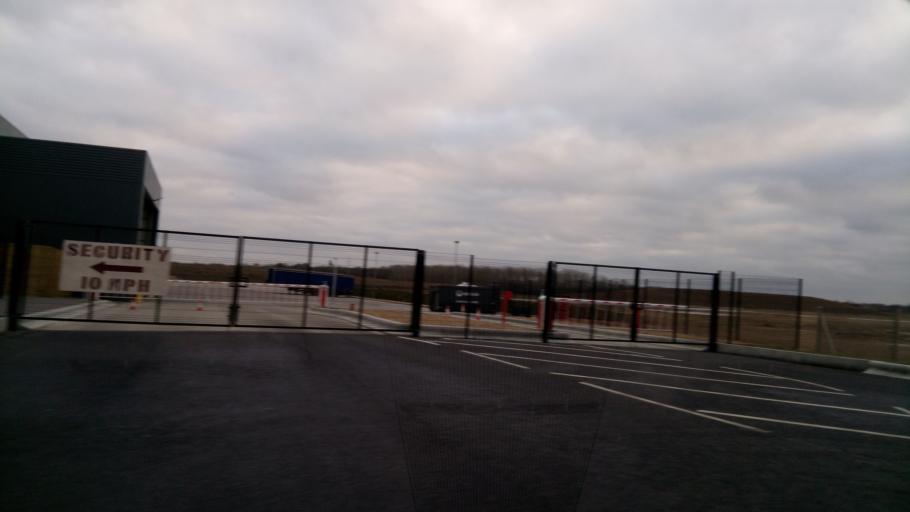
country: GB
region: England
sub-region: Cambridgeshire
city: Yaxley
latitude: 52.5317
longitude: -0.2987
